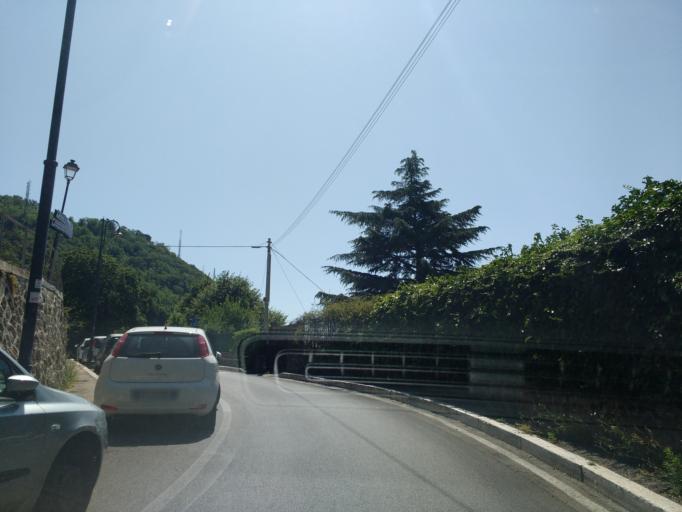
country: IT
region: Latium
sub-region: Citta metropolitana di Roma Capitale
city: Rocca di Papa
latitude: 41.7564
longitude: 12.7067
